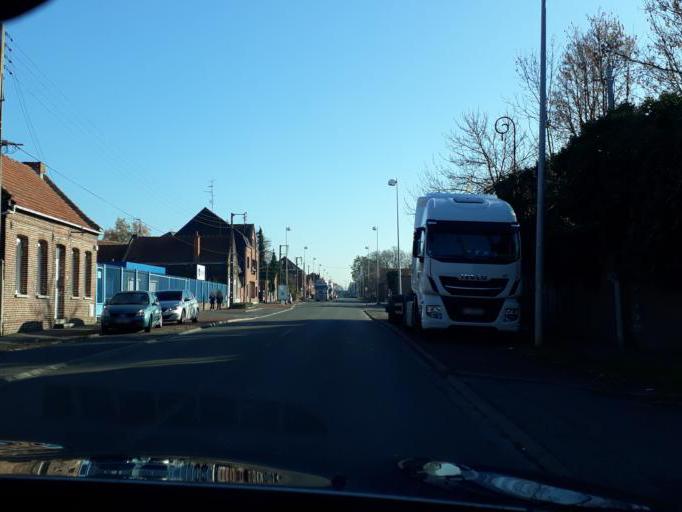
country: FR
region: Nord-Pas-de-Calais
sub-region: Departement du Nord
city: Auberchicourt
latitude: 50.3328
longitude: 3.2383
